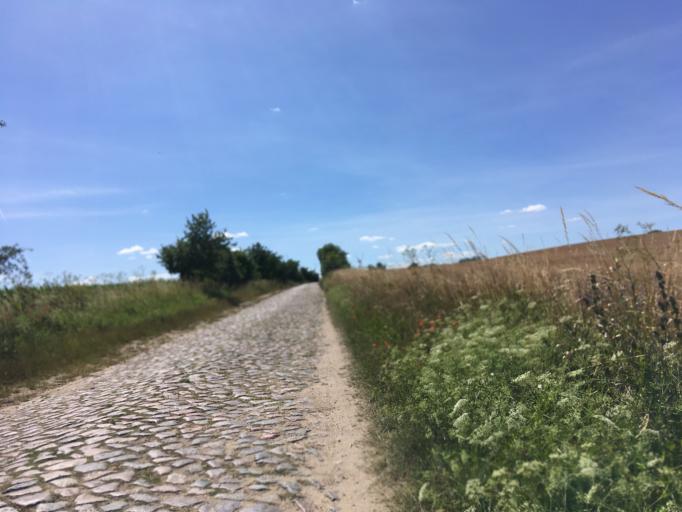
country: DE
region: Brandenburg
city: Brussow
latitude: 53.3210
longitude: 14.1123
